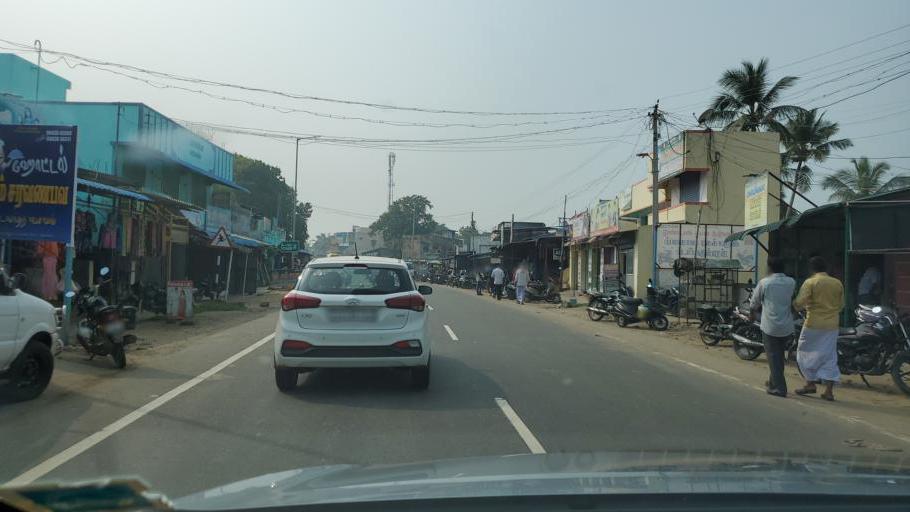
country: IN
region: Tamil Nadu
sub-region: Ariyalur
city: Ariyalur
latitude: 11.2350
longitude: 79.0220
